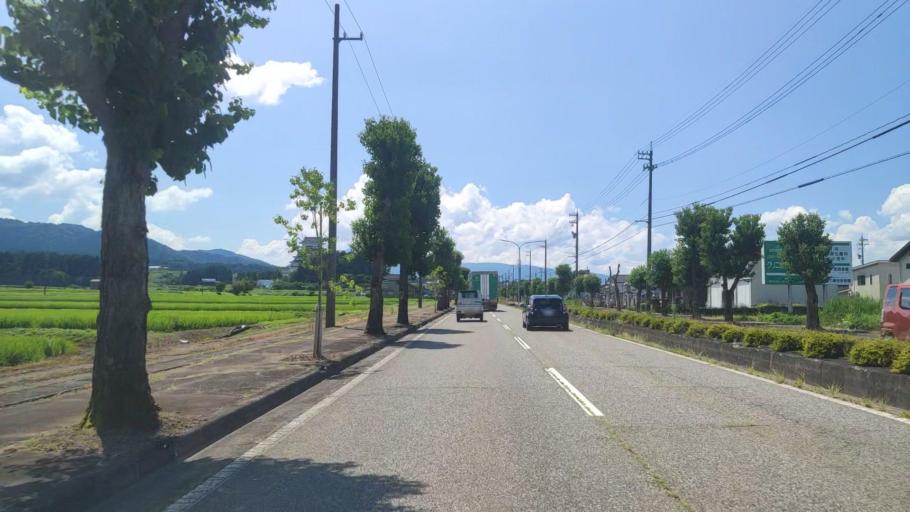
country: JP
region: Fukui
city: Katsuyama
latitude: 36.0483
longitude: 136.5154
